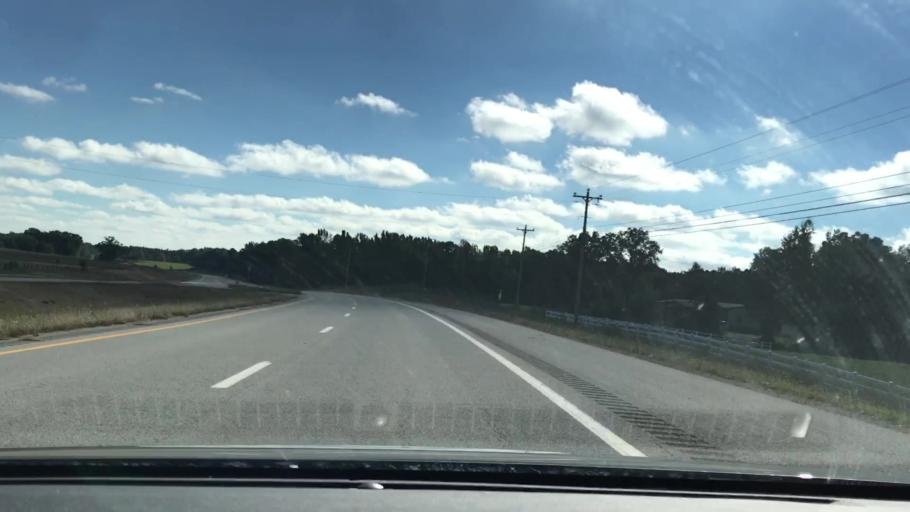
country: US
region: Tennessee
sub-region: Fentress County
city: Grimsley
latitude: 36.3101
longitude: -84.9743
